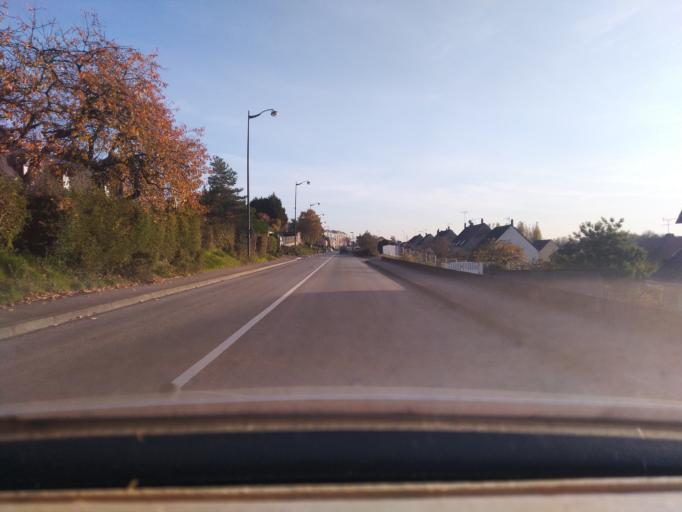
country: FR
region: Haute-Normandie
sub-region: Departement de la Seine-Maritime
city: Le Trait
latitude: 49.4790
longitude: 0.8107
